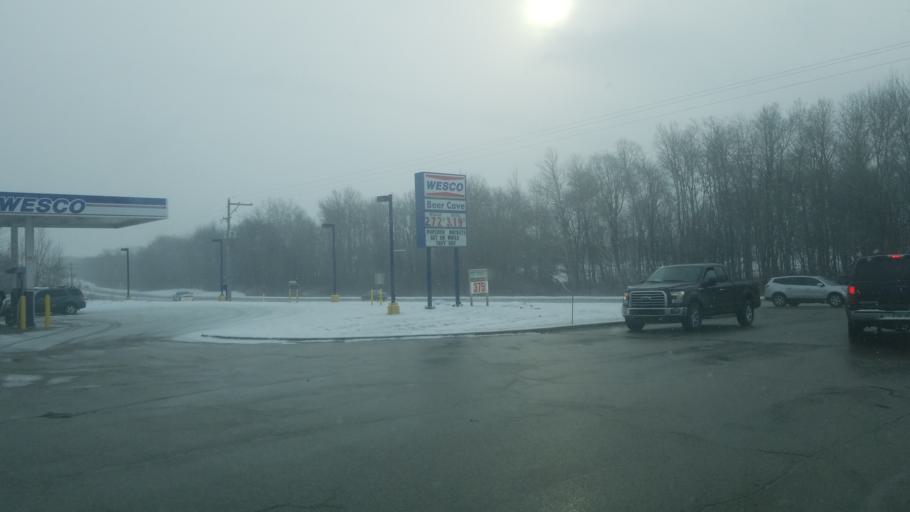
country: US
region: Michigan
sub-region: Mecosta County
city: Big Rapids
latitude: 43.6889
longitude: -85.5093
